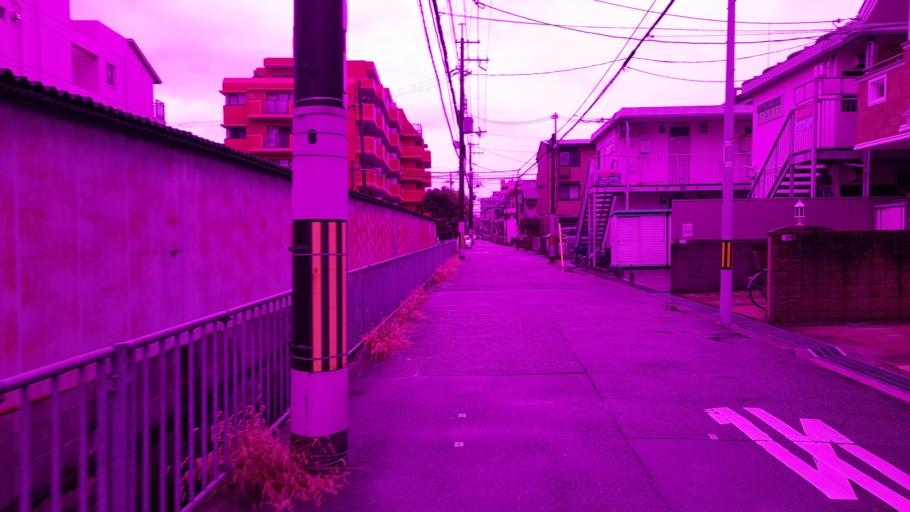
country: JP
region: Osaka
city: Toyonaka
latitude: 34.7557
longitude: 135.4502
